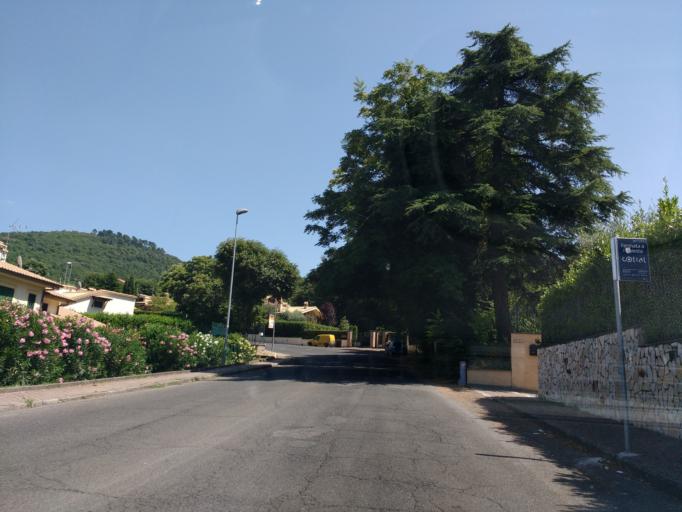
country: IT
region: Latium
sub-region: Citta metropolitana di Roma Capitale
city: Rocca di Papa
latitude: 41.7696
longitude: 12.7077
